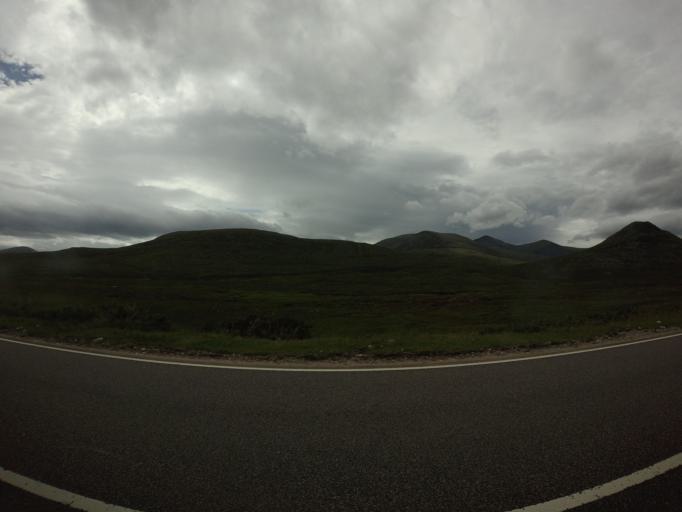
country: GB
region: Scotland
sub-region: Highland
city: Ullapool
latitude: 57.7373
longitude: -4.9555
